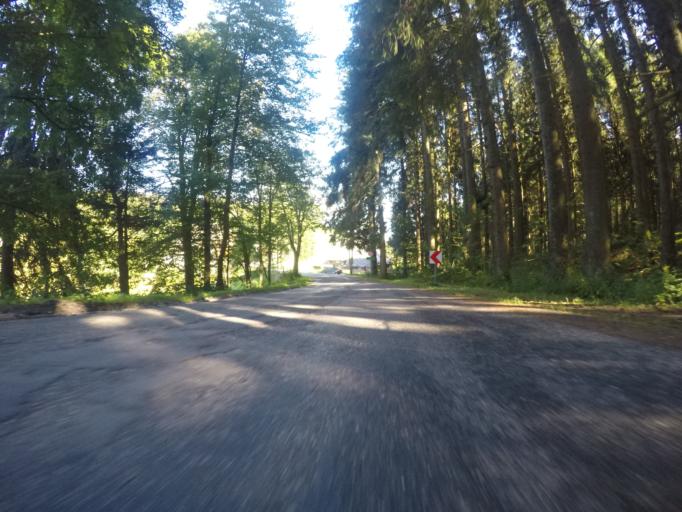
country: DE
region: Baden-Wuerttemberg
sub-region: Freiburg Region
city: Gutenbach
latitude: 48.0630
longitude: 8.1747
